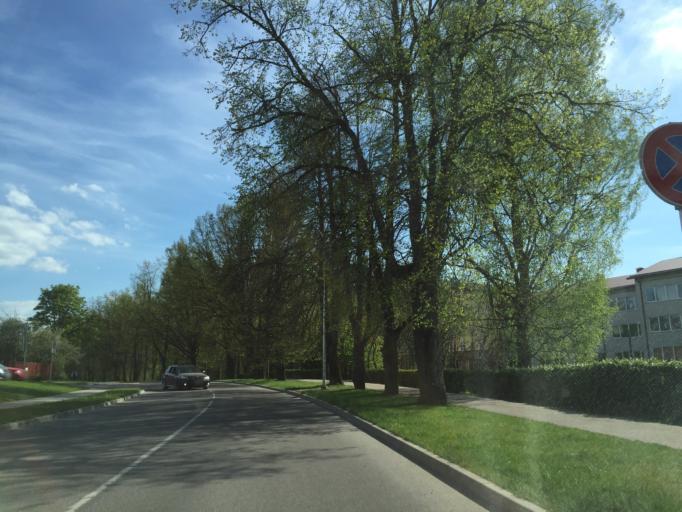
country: LV
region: Limbazu Rajons
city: Limbazi
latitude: 57.5081
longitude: 24.7138
